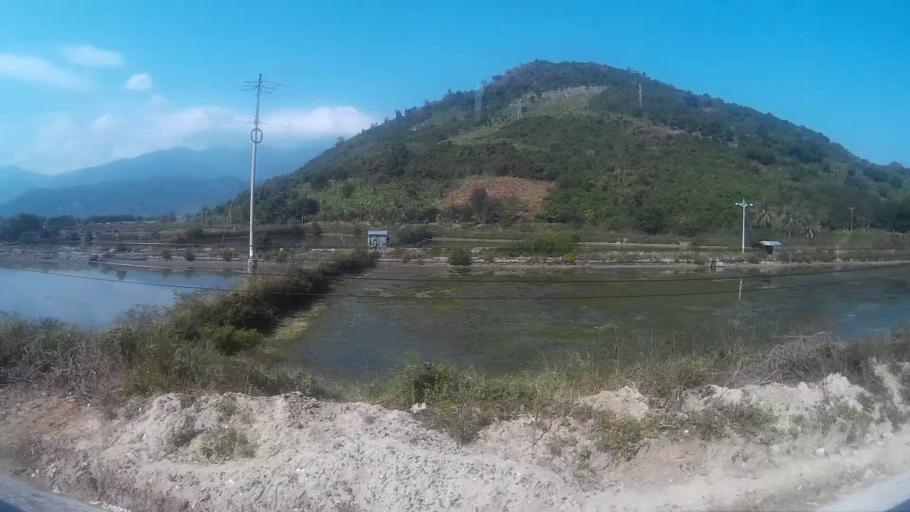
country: VN
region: Khanh Hoa
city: Ninh Hoa
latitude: 12.4146
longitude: 109.1491
